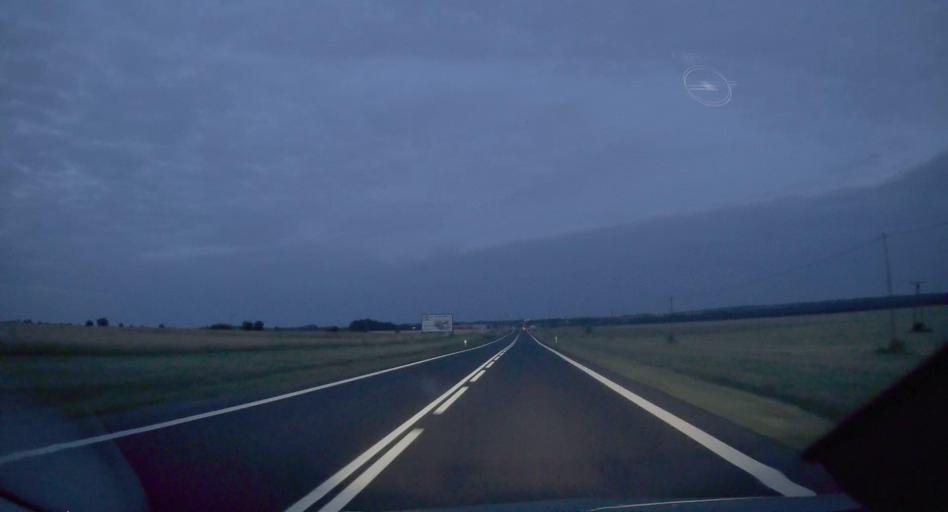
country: PL
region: Silesian Voivodeship
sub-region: Powiat klobucki
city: Klobuck
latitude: 50.8930
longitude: 18.9595
